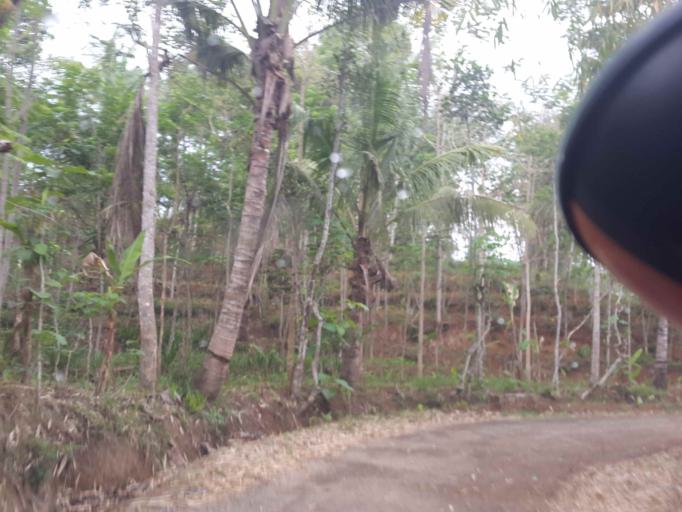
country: ID
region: East Java
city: Krajan Tengah
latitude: -7.9742
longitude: 111.3092
